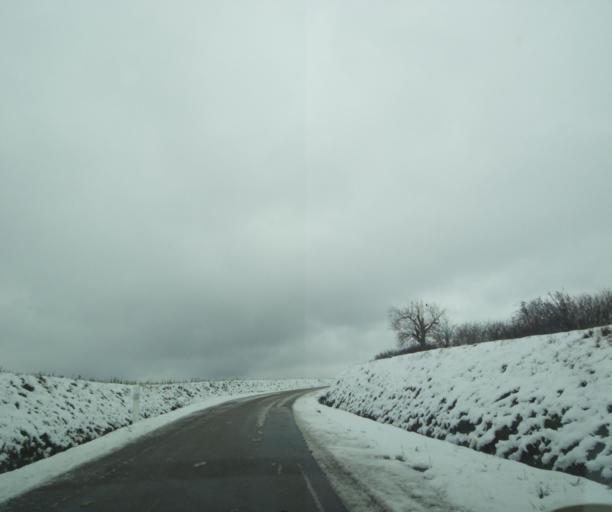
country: FR
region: Champagne-Ardenne
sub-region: Departement de la Haute-Marne
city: Laneuville-a-Remy
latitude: 48.4050
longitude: 4.8523
